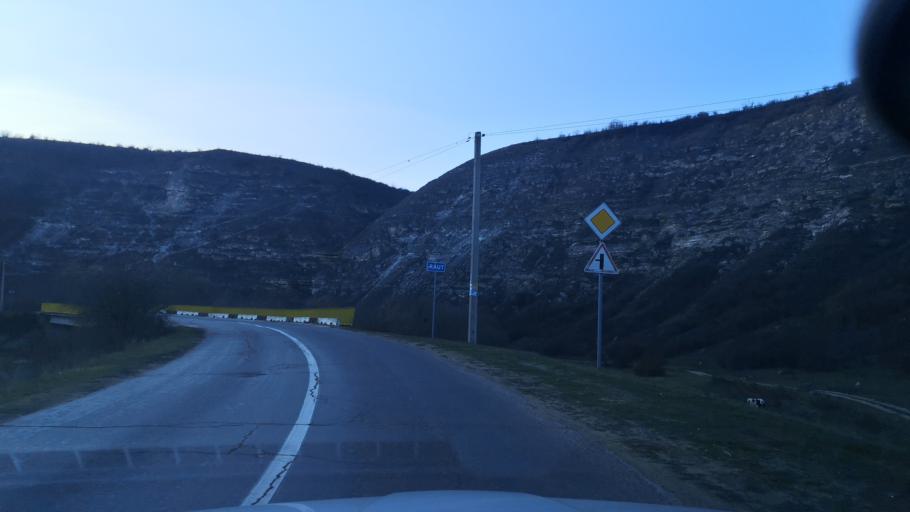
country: MD
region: Telenesti
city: Cocieri
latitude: 47.3077
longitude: 28.9633
